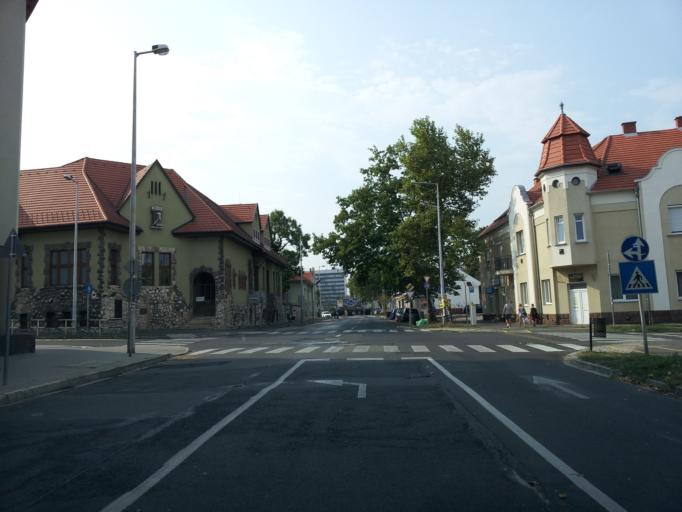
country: HU
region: Gyor-Moson-Sopron
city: Gyor
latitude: 47.6814
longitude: 17.6387
